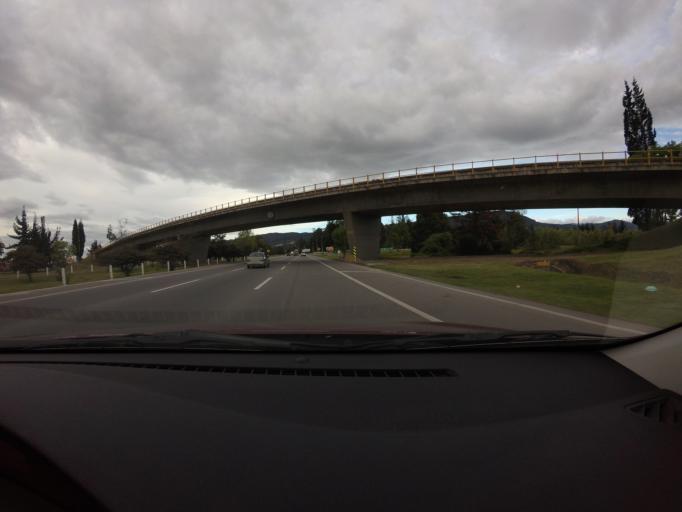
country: CO
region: Cundinamarca
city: Sopo
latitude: 4.9390
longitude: -73.9664
